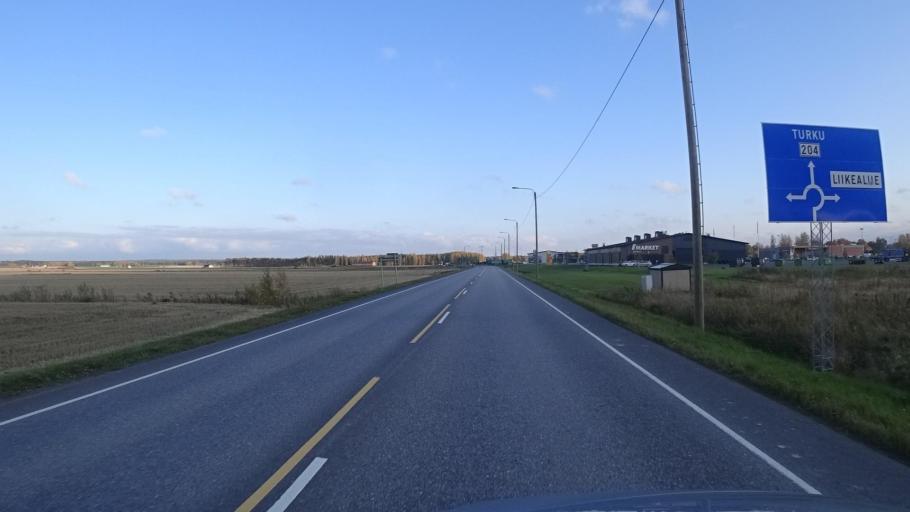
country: FI
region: Satakunta
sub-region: Rauma
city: Saekylae
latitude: 61.0480
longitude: 22.3541
